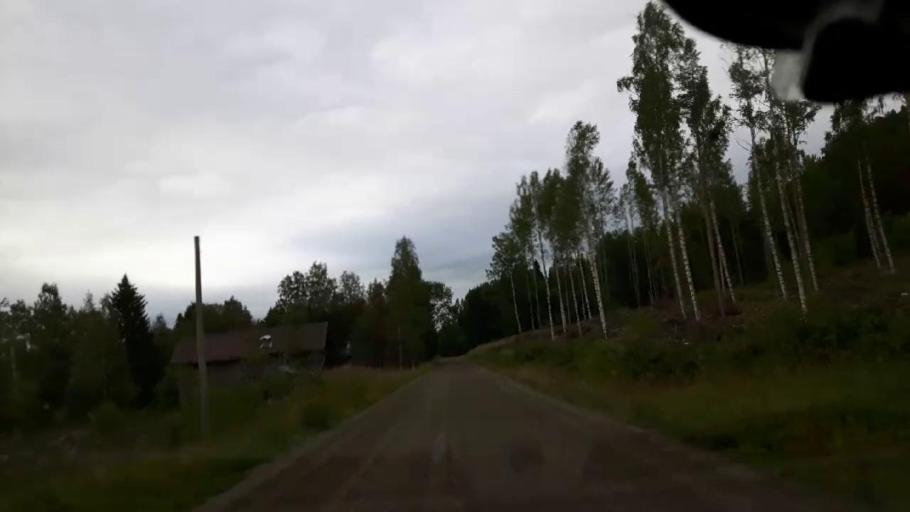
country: SE
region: Jaemtland
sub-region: Braecke Kommun
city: Braecke
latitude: 62.9077
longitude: 15.5914
